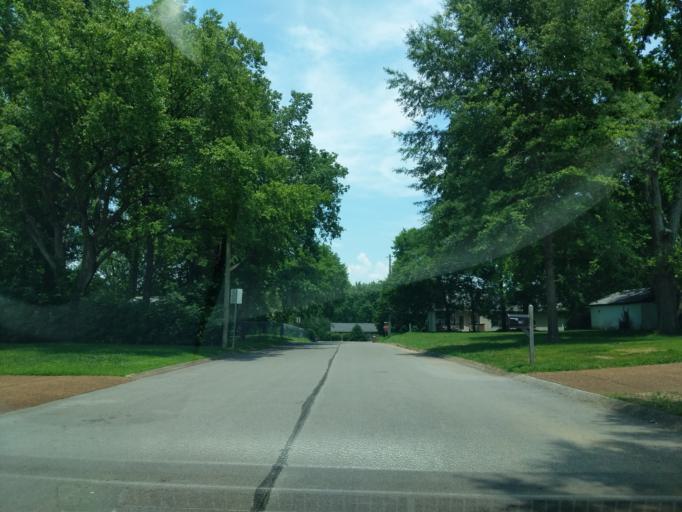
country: US
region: Tennessee
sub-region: Davidson County
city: Lakewood
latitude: 36.2378
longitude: -86.6386
